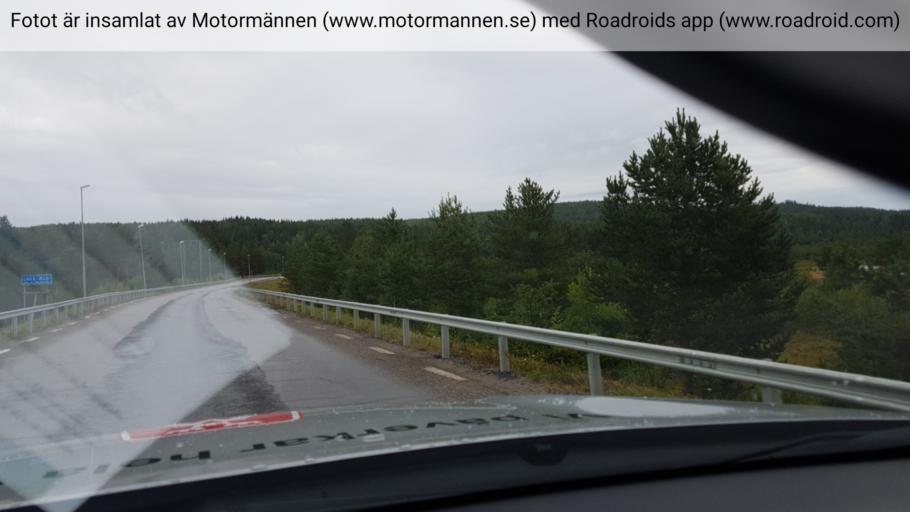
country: SE
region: Norrbotten
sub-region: Alvsbyns Kommun
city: AElvsbyn
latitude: 66.0919
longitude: 20.9256
